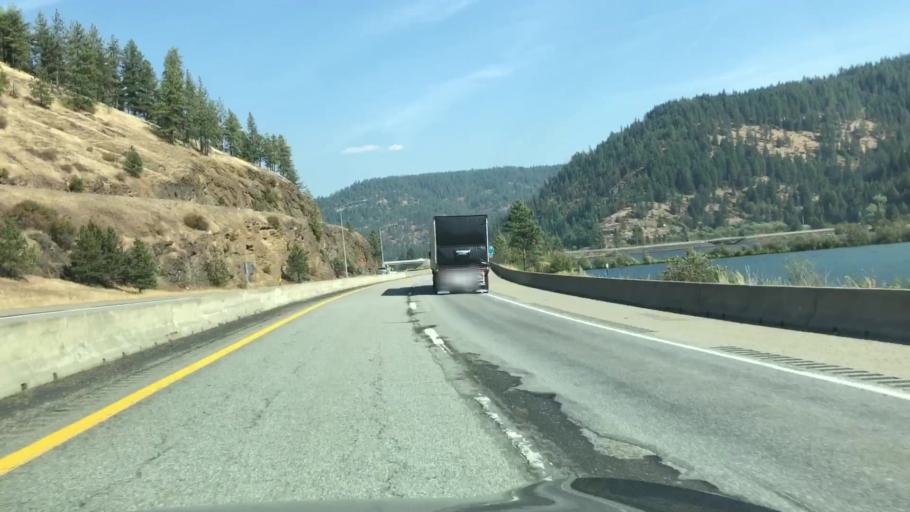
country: US
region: Idaho
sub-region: Kootenai County
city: Coeur d'Alene
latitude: 47.6237
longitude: -116.6574
